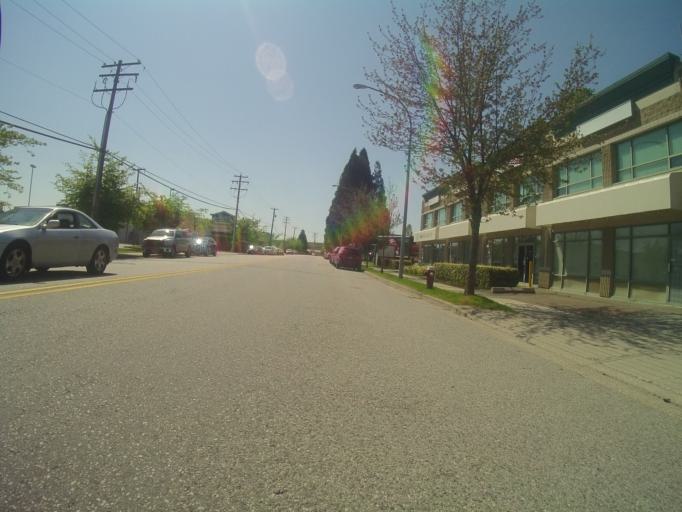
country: CA
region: British Columbia
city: Richmond
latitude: 49.1946
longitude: -123.0834
